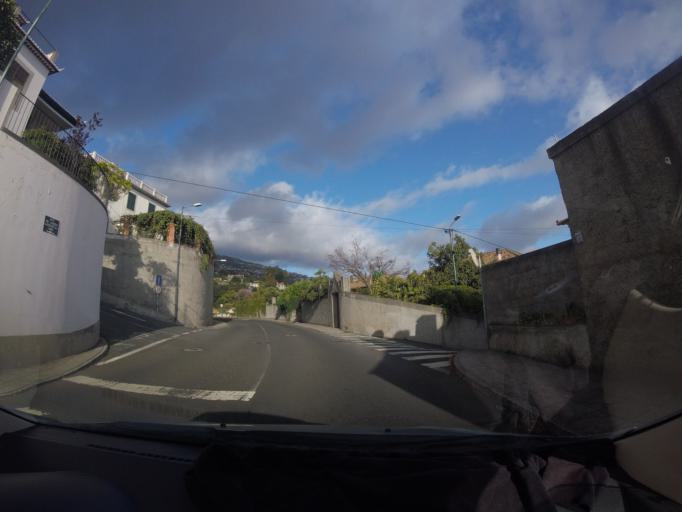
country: PT
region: Madeira
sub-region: Funchal
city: Nossa Senhora do Monte
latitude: 32.6576
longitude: -16.9108
